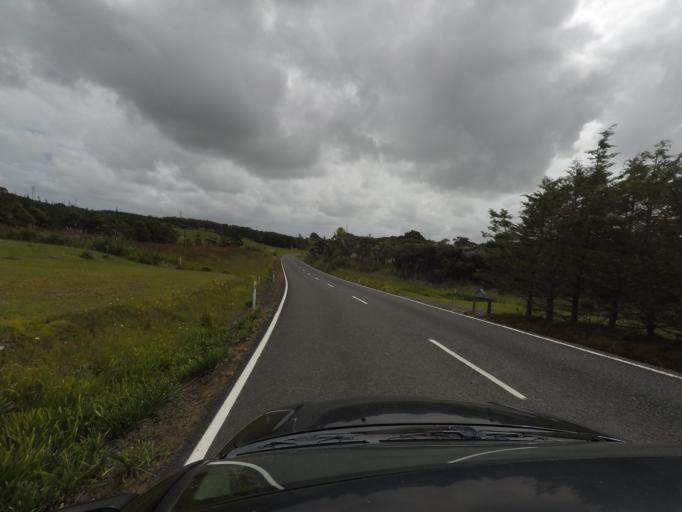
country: NZ
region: Auckland
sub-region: Auckland
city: Parakai
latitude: -36.5061
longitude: 174.4655
